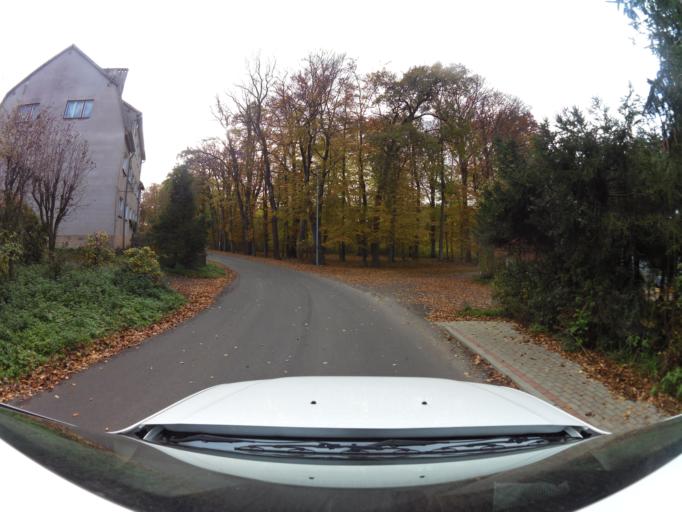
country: PL
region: West Pomeranian Voivodeship
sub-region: Powiat gryficki
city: Gryfice
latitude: 53.9807
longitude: 15.2106
